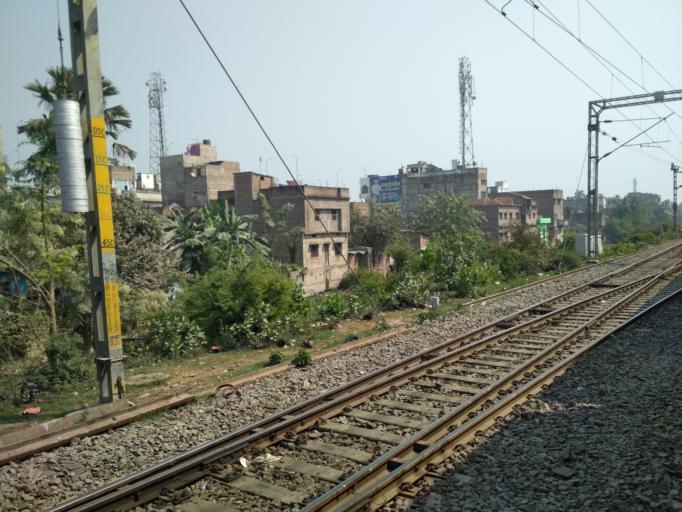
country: IN
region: Bihar
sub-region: Khagaria
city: Khagaria
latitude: 25.5064
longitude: 86.4727
